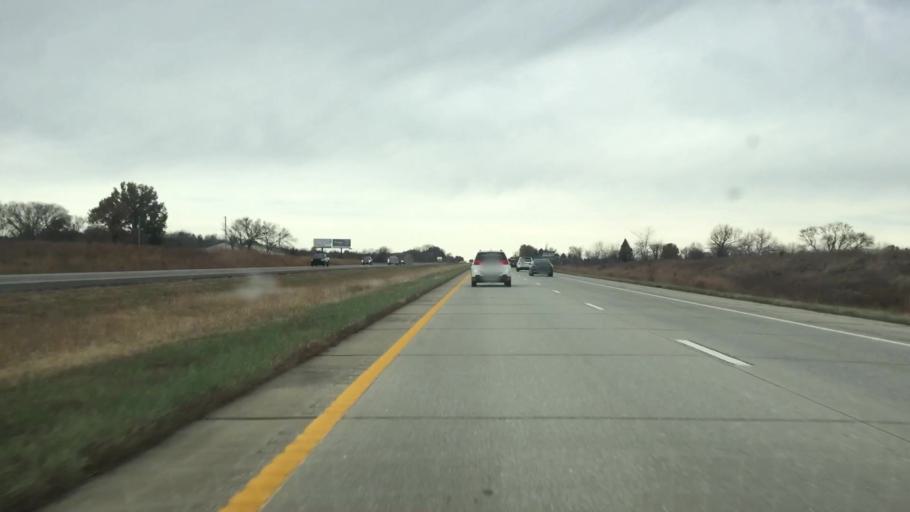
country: US
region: Missouri
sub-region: Saint Clair County
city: Osceola
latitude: 38.0907
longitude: -93.7076
